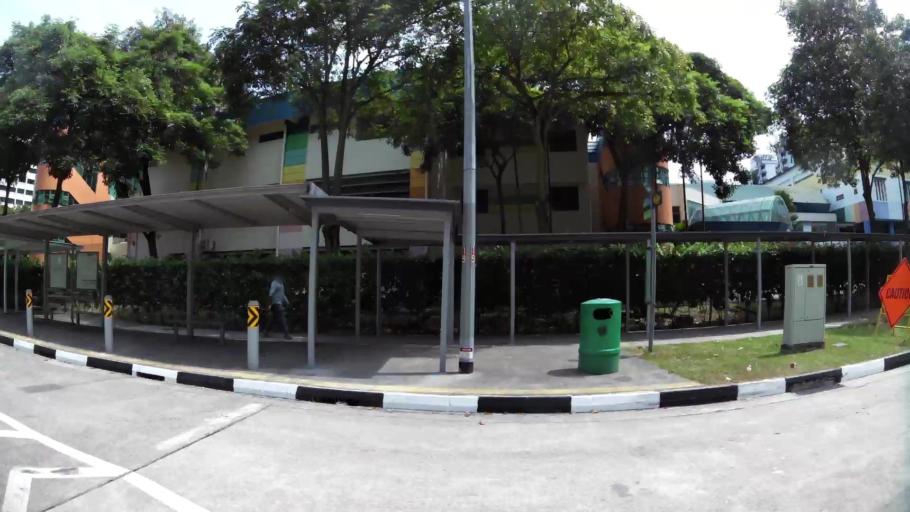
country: MY
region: Johor
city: Johor Bahru
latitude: 1.3392
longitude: 103.6984
